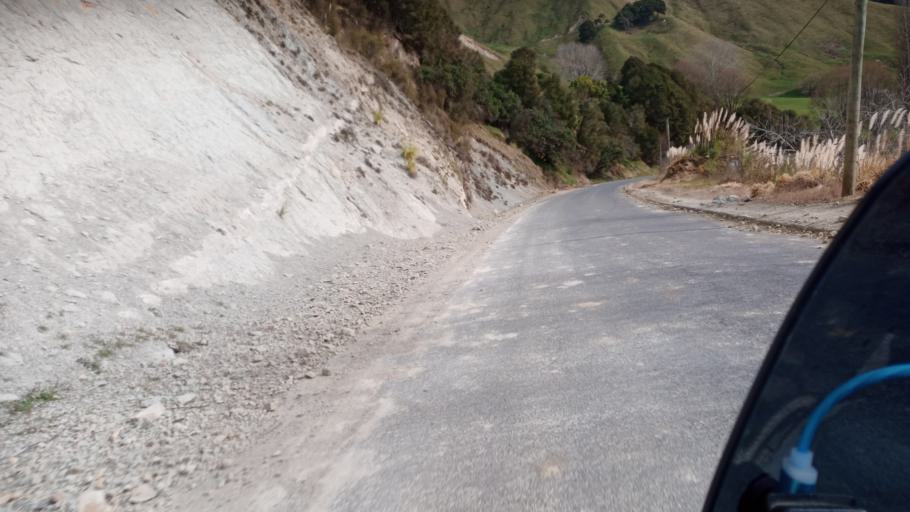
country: NZ
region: Hawke's Bay
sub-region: Wairoa District
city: Wairoa
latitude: -38.7967
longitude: 177.4407
